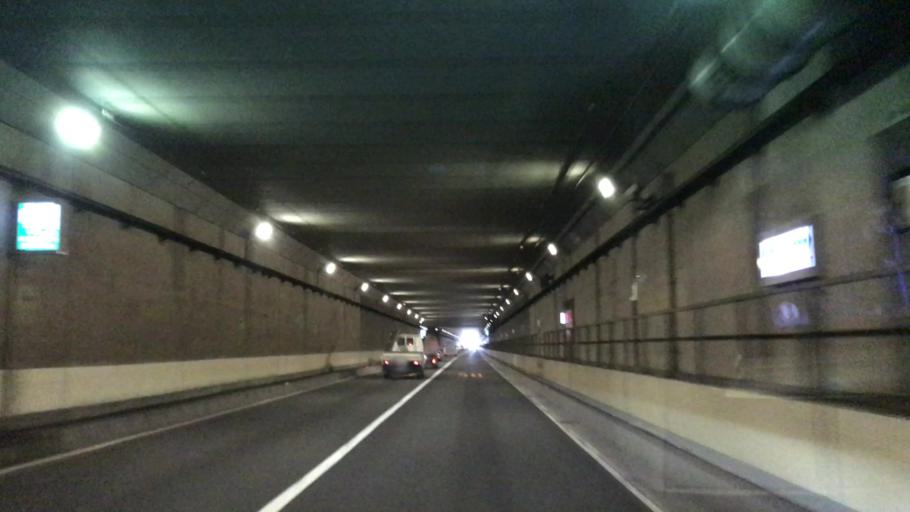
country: JP
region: Hokkaido
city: Sapporo
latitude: 43.0603
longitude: 141.3573
